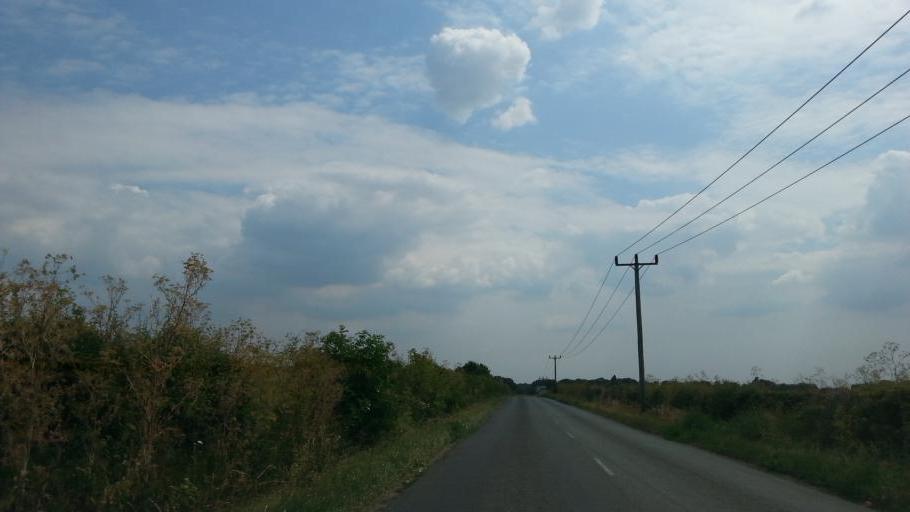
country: GB
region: England
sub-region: Suffolk
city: Lakenheath
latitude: 52.3722
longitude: 0.5368
